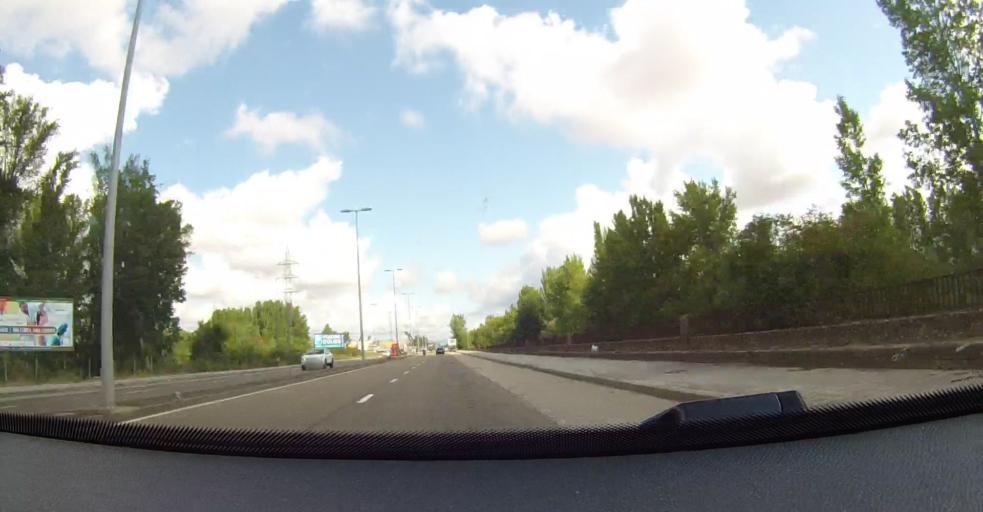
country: ES
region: Castille and Leon
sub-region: Provincia de Leon
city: Leon
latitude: 42.5776
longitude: -5.5703
